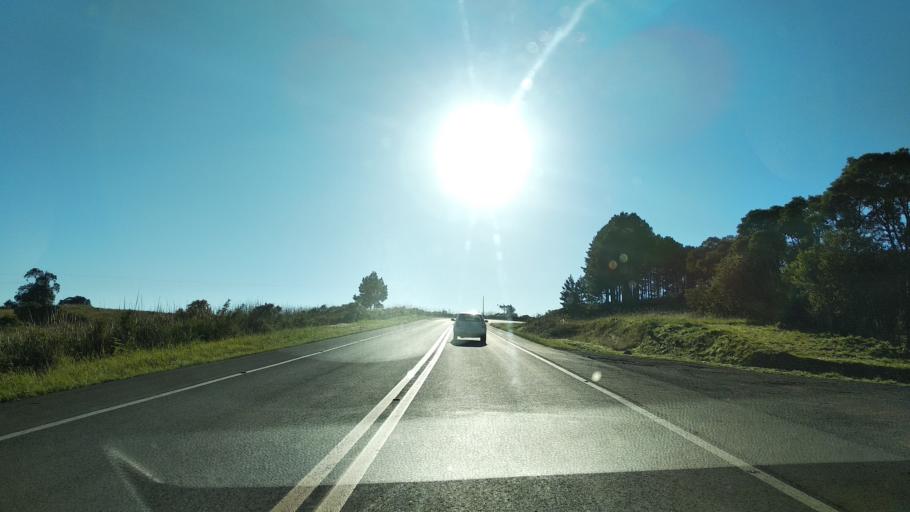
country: BR
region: Santa Catarina
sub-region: Lages
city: Lages
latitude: -27.7881
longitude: -50.4279
